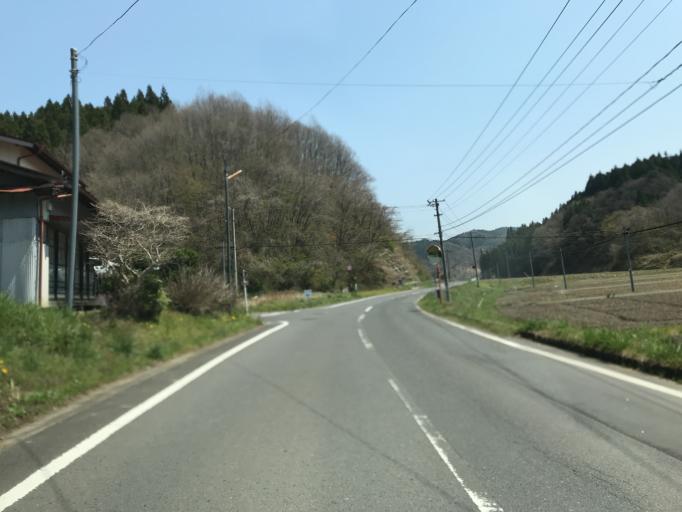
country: JP
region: Fukushima
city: Ishikawa
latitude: 37.0467
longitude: 140.4967
